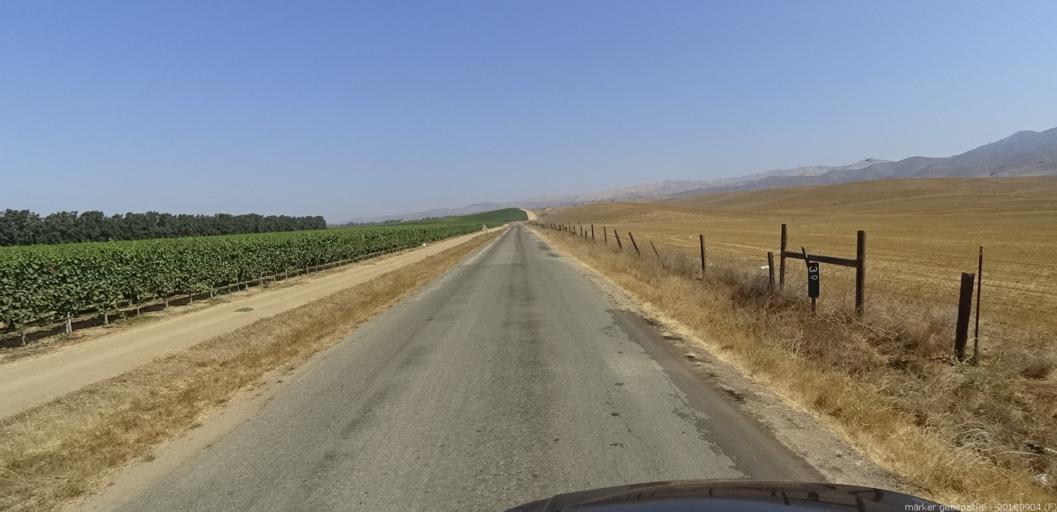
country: US
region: California
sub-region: Monterey County
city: Soledad
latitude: 36.4838
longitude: -121.3567
